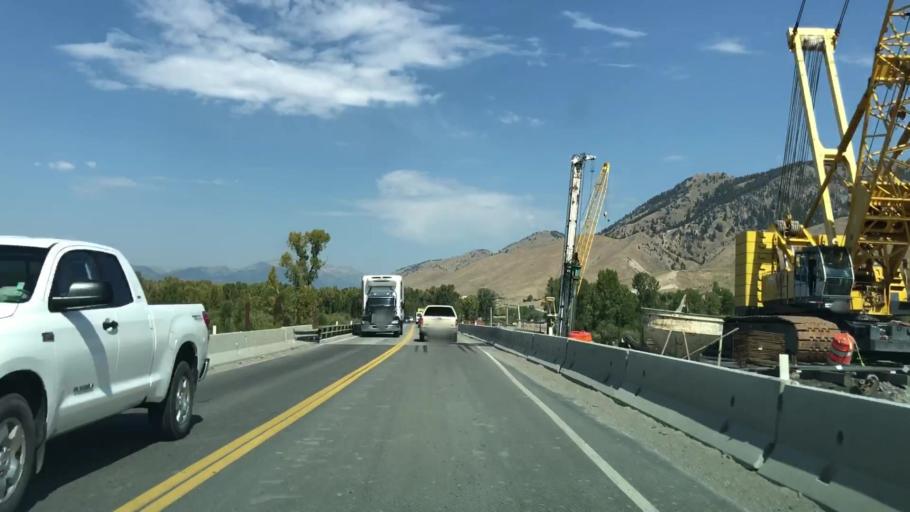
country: US
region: Wyoming
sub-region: Teton County
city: South Park
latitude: 43.3836
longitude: -110.7448
